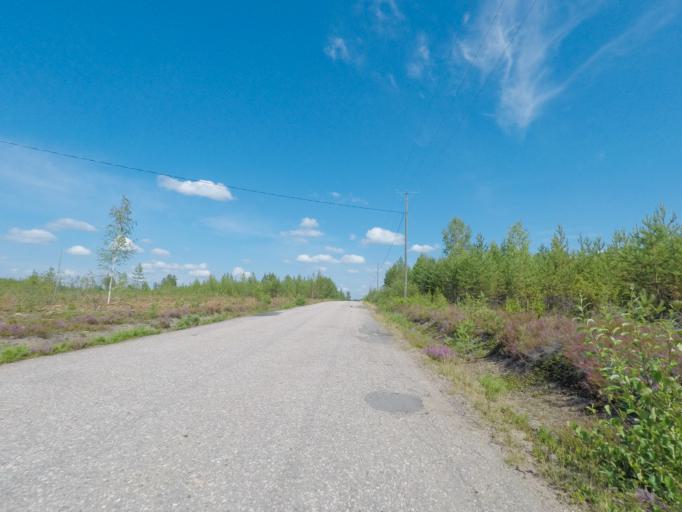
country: FI
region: Southern Savonia
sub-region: Mikkeli
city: Puumala
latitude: 61.4269
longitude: 28.1606
